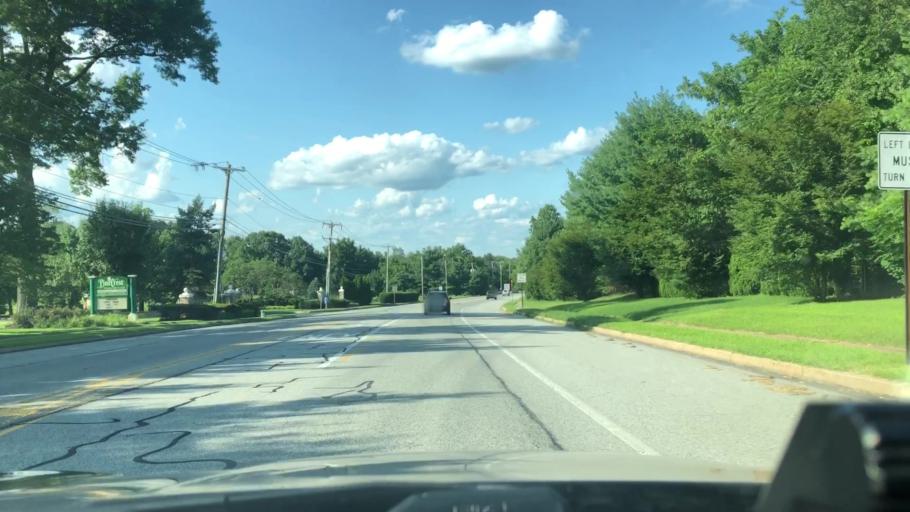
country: US
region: Pennsylvania
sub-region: Montgomery County
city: Montgomeryville
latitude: 40.2546
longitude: -75.2378
